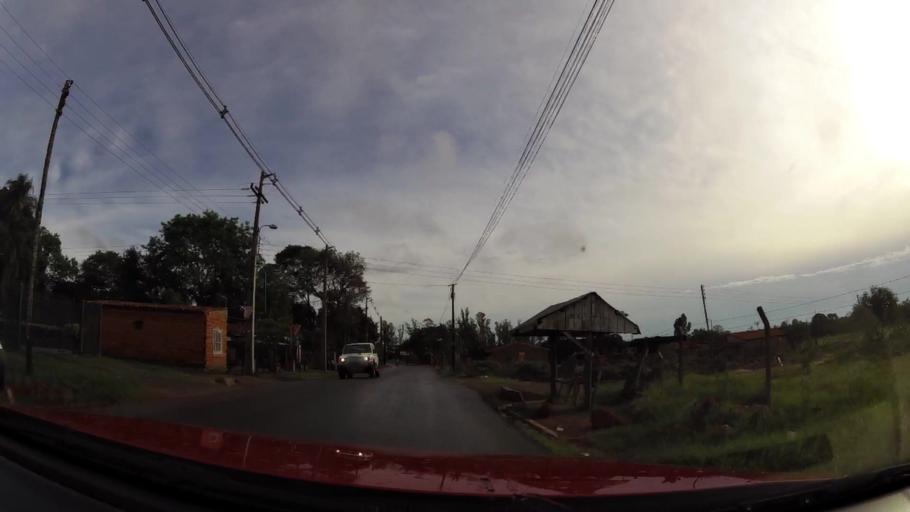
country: PY
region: Central
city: Limpio
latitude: -25.1984
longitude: -57.5032
